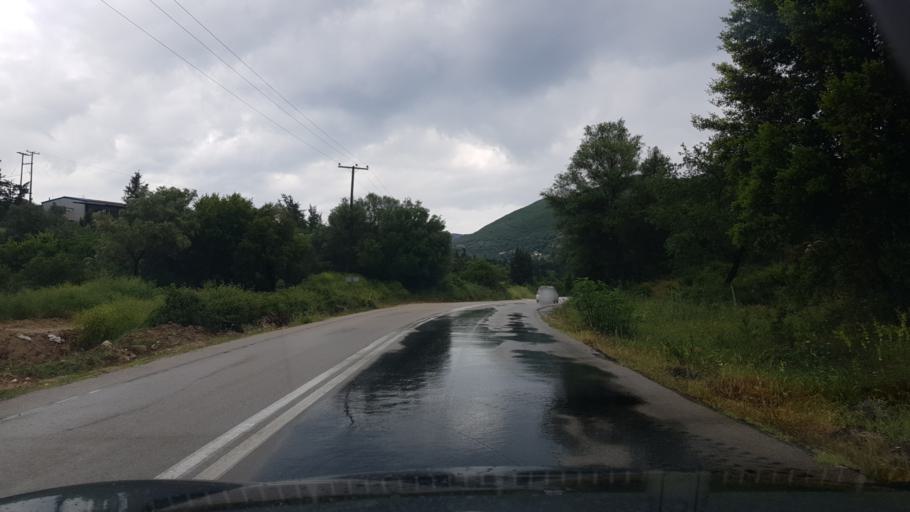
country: GR
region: Ionian Islands
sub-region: Lefkada
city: Nidri
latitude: 38.6297
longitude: 20.6341
